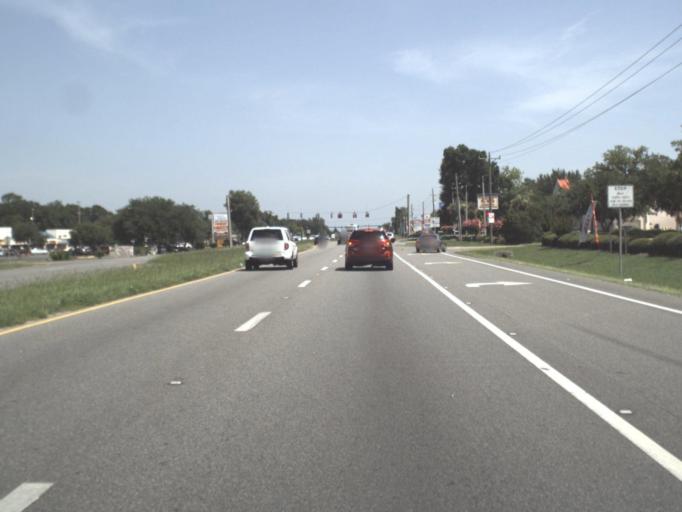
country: US
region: Florida
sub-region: Levy County
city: Chiefland
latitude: 29.4994
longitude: -82.8697
